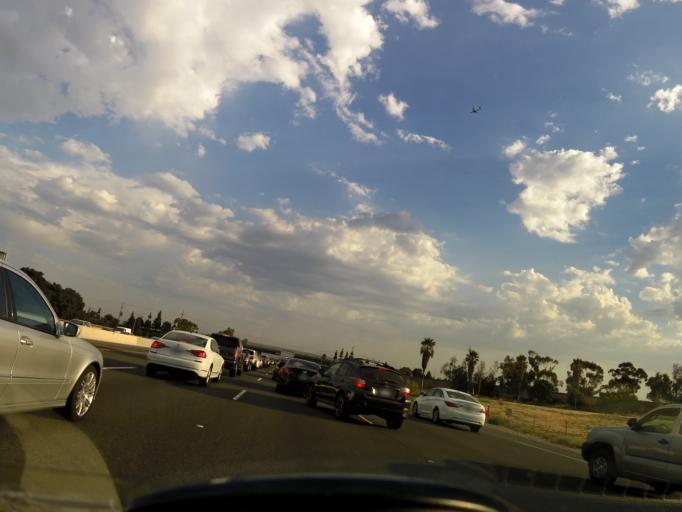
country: US
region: California
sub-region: Orange County
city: Orange
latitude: 33.7762
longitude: -117.8312
